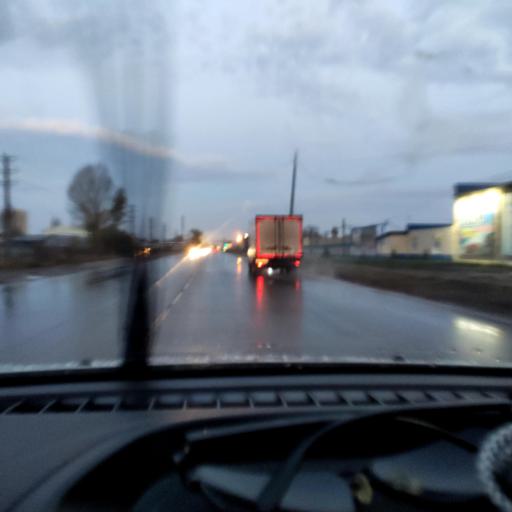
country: RU
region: Samara
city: Tol'yatti
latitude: 53.5301
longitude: 49.4667
